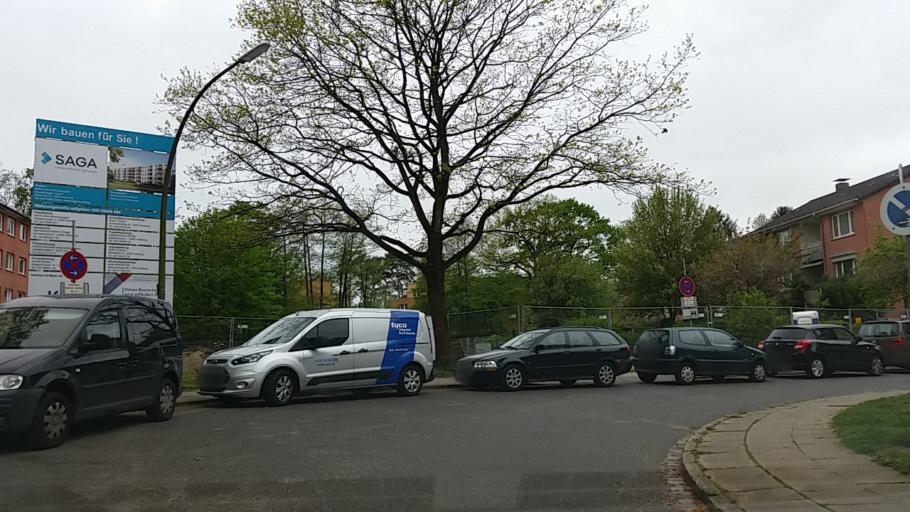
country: DE
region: Schleswig-Holstein
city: Halstenbek
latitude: 53.5777
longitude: 9.8312
